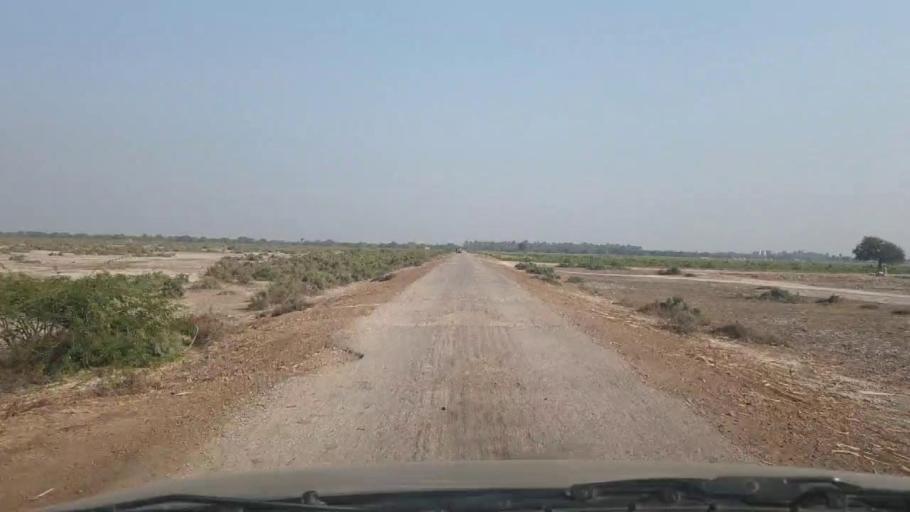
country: PK
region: Sindh
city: Digri
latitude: 25.2646
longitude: 69.1689
